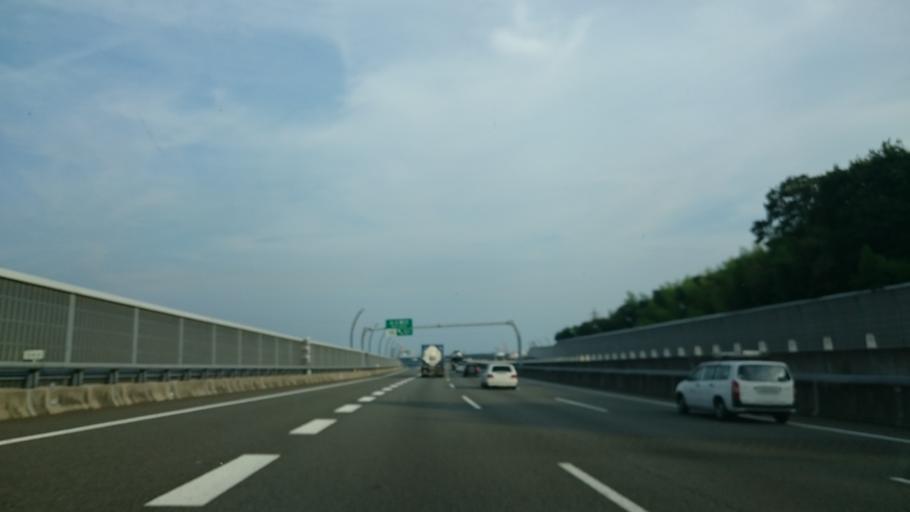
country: JP
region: Mie
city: Yokkaichi
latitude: 35.0331
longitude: 136.6436
